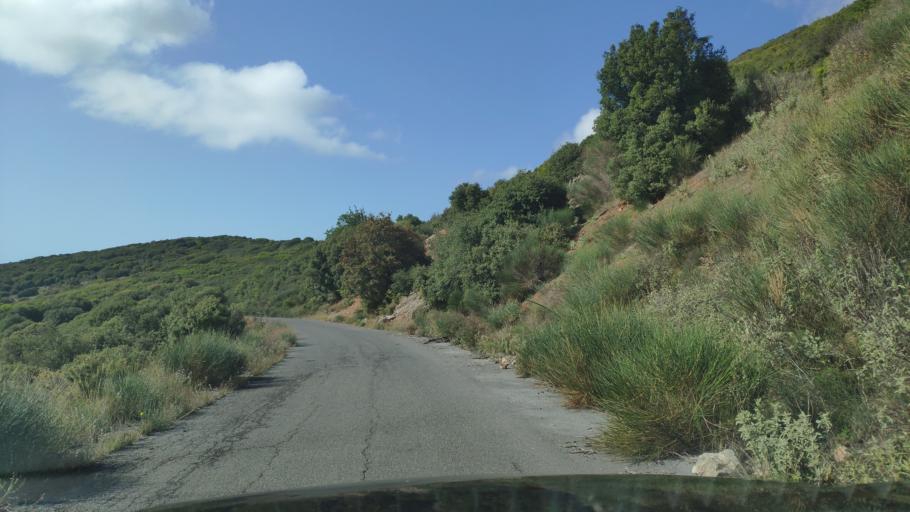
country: GR
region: Peloponnese
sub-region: Nomos Arkadias
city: Dimitsana
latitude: 37.5735
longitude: 22.0041
